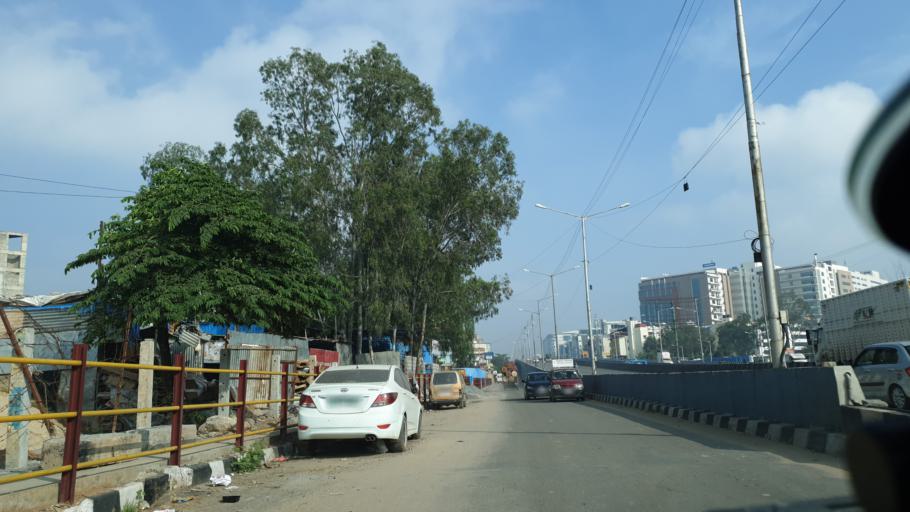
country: IN
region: Karnataka
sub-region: Bangalore Urban
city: Bangalore
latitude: 12.9761
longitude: 77.6966
